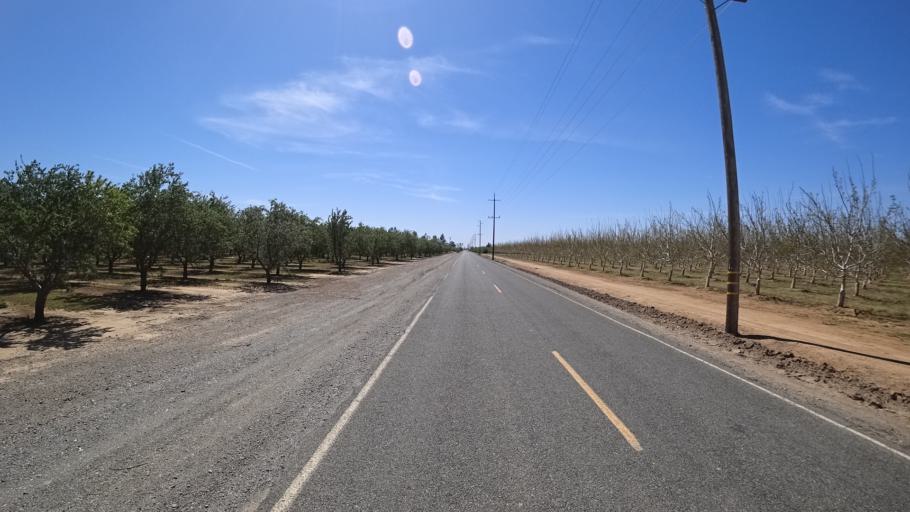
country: US
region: California
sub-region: Glenn County
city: Orland
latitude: 39.7054
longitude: -122.1781
